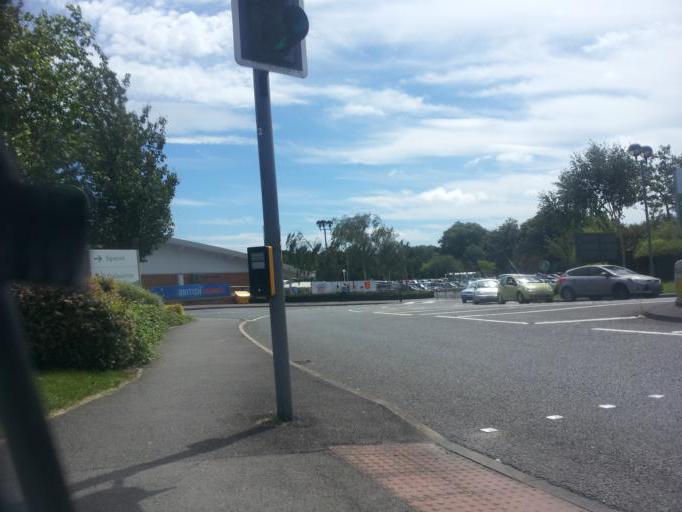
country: GB
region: England
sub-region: Kent
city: Chatham
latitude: 51.3450
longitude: 0.5075
